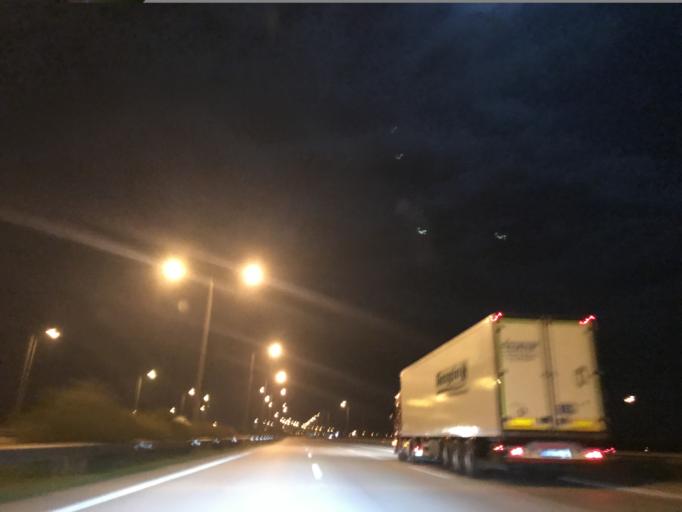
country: TR
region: Hatay
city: Mahmutlar
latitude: 36.9583
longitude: 36.1343
